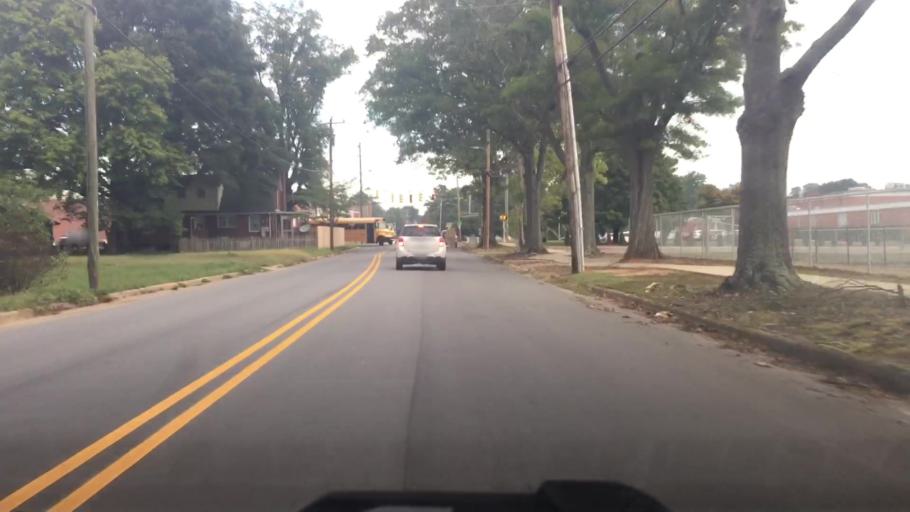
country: US
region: North Carolina
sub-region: Iredell County
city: Mooresville
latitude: 35.5750
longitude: -80.8012
